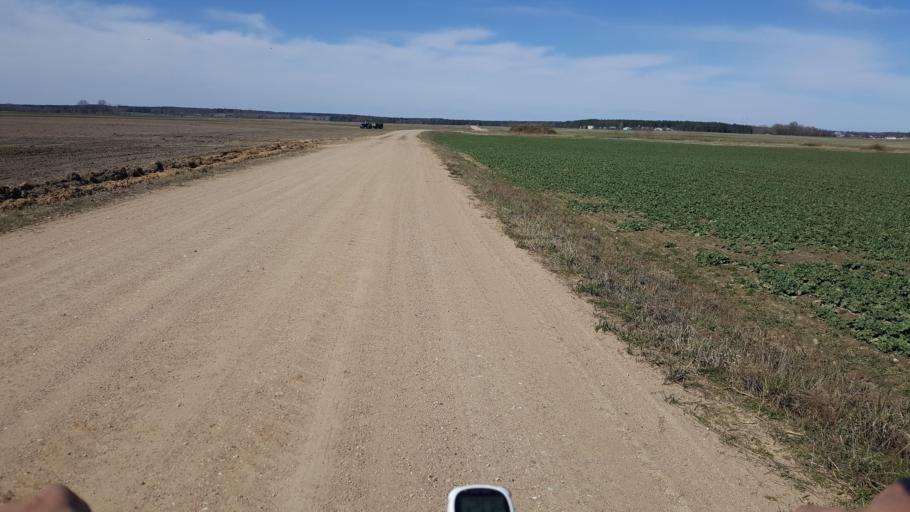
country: BY
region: Brest
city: Kamyanyets
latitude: 52.3007
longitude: 23.9080
